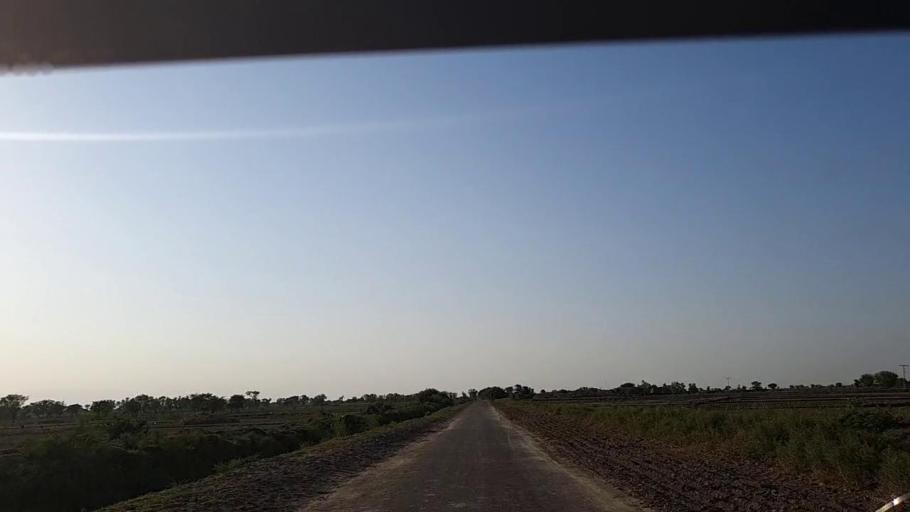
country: PK
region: Sindh
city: Johi
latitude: 26.7416
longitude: 67.5983
